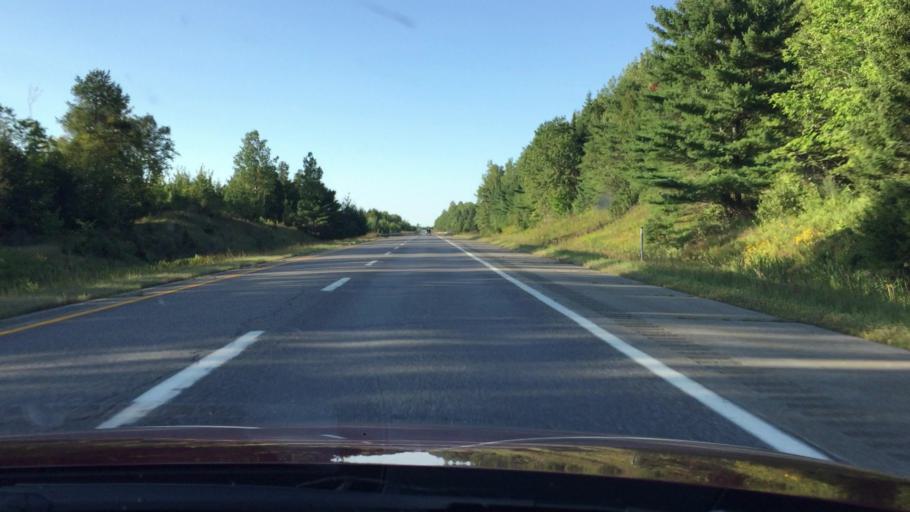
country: US
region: Maine
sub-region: Penobscot County
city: Medway
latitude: 45.6462
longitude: -68.4984
